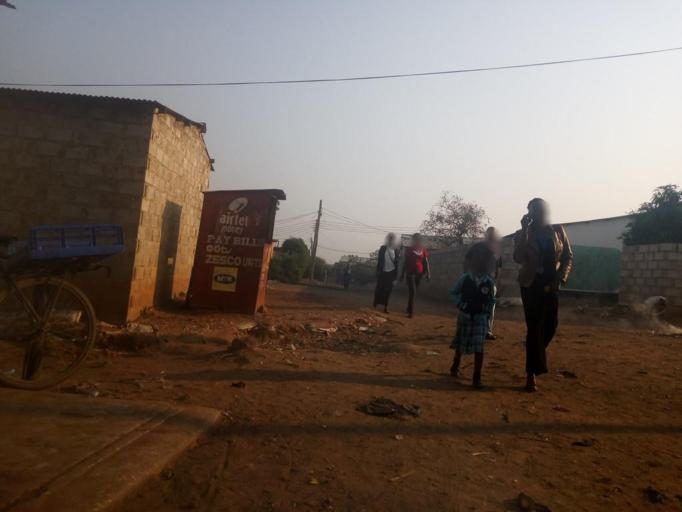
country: ZM
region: Lusaka
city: Lusaka
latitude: -15.4069
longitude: 28.3631
